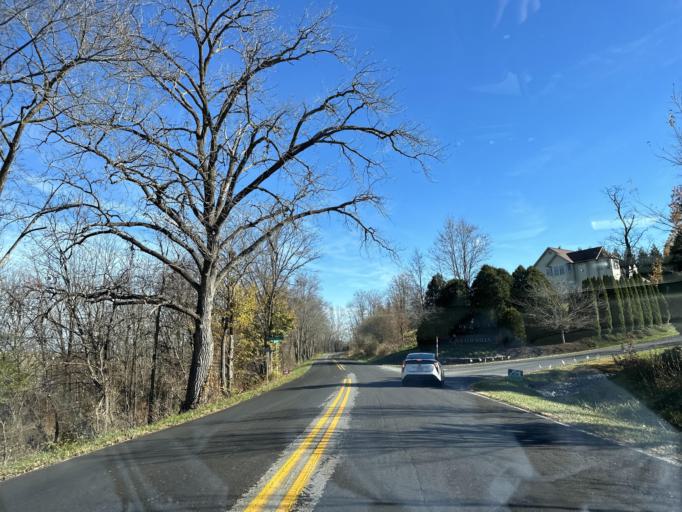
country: US
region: Virginia
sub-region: Augusta County
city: Fishersville
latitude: 38.1138
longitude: -78.9591
